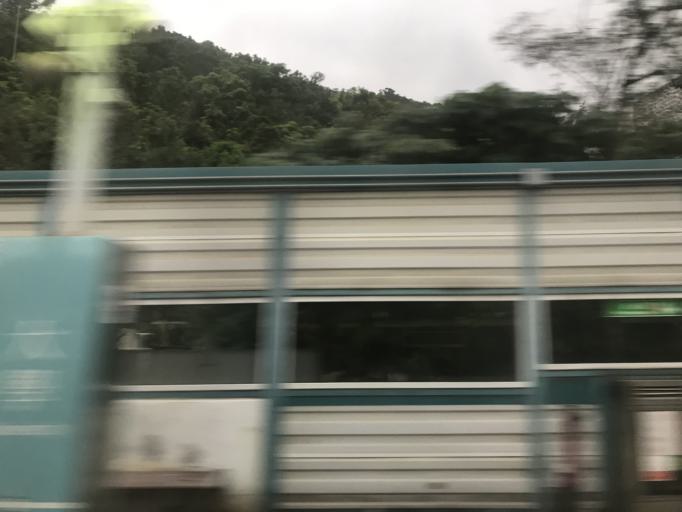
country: HK
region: Sha Tin
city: Sha Tin
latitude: 22.4129
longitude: 114.2099
